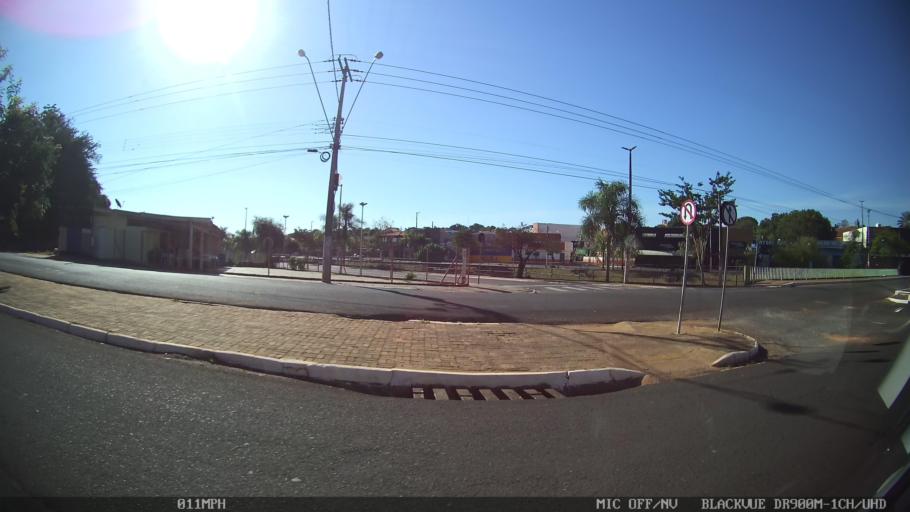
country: BR
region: Sao Paulo
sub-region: Olimpia
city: Olimpia
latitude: -20.7441
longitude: -48.9051
